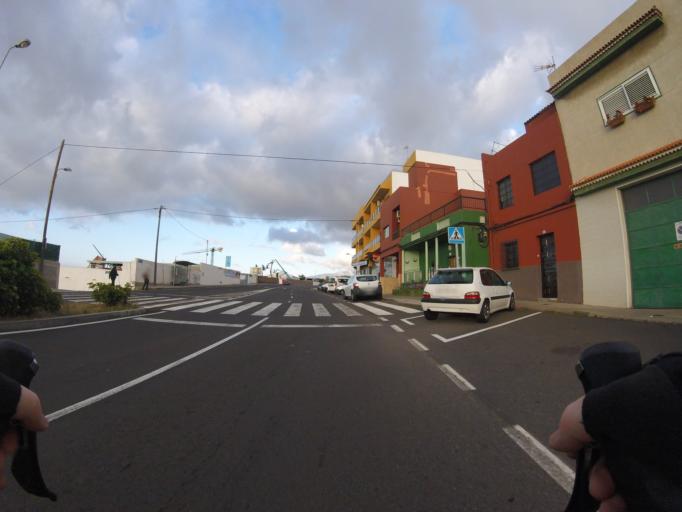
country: ES
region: Canary Islands
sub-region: Provincia de Santa Cruz de Tenerife
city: La Laguna
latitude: 28.4275
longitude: -16.3137
